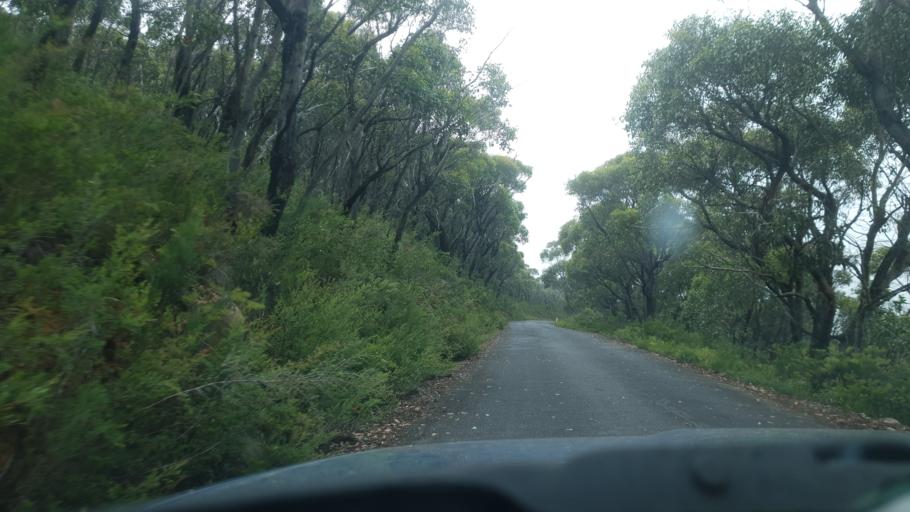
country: AU
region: Victoria
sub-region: Northern Grampians
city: Stawell
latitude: -37.2701
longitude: 142.5792
